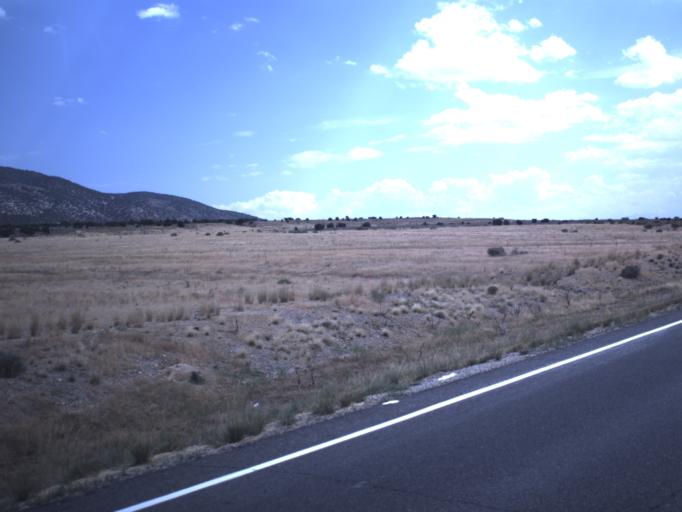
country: US
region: Utah
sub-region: Tooele County
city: Tooele
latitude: 40.3068
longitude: -112.2795
